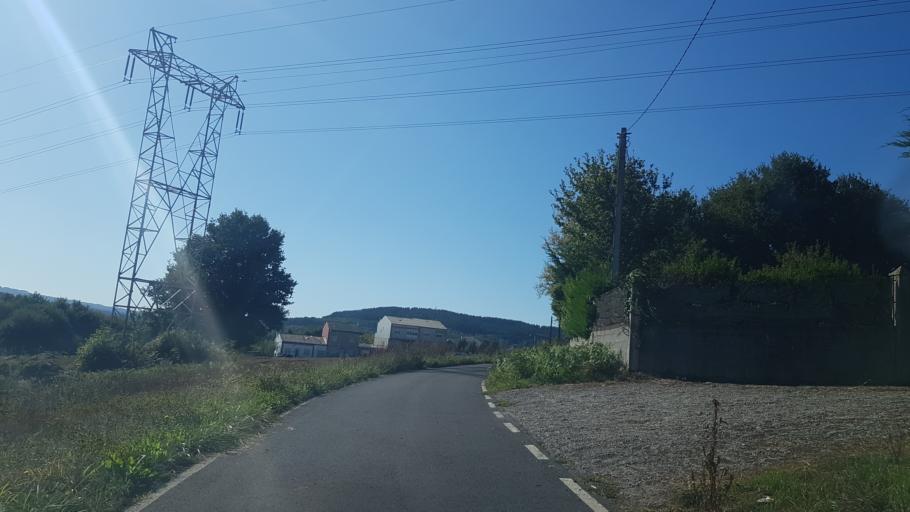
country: ES
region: Galicia
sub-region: Provincia de Lugo
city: Lugo
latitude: 43.0125
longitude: -7.5767
